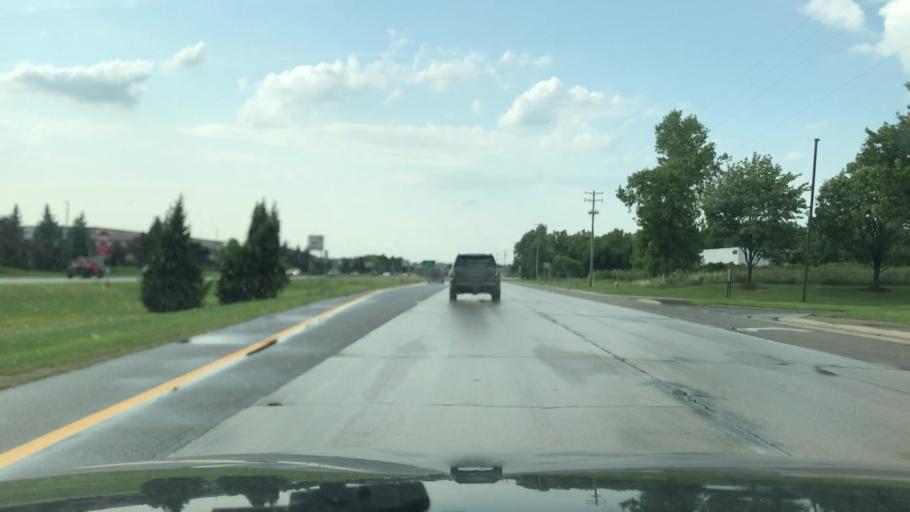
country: US
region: Michigan
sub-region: Kent County
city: East Grand Rapids
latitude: 42.8777
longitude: -85.5604
